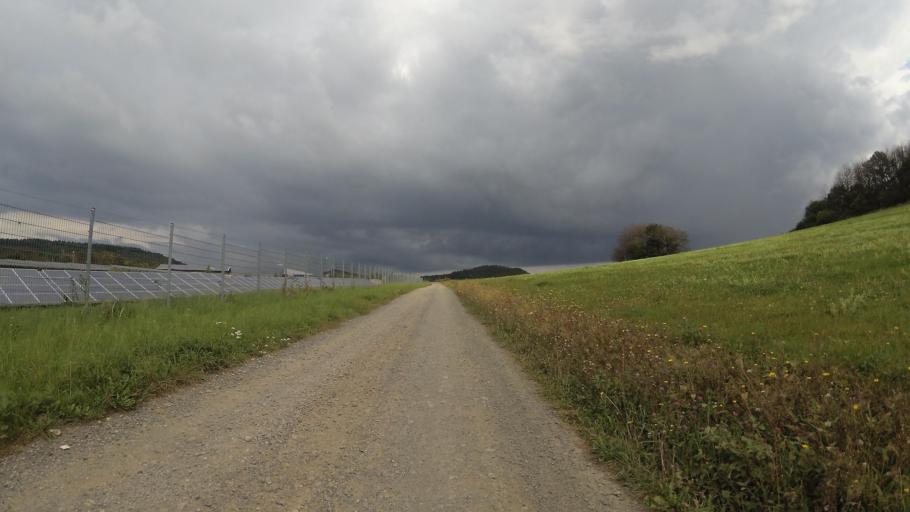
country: DE
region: Saarland
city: Freisen
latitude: 49.5222
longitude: 7.2209
